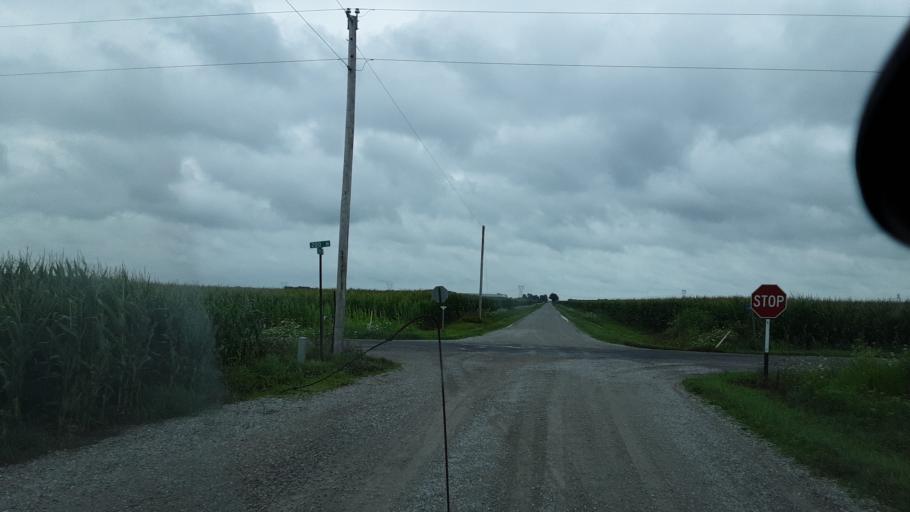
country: US
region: Indiana
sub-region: Wells County
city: Bluffton
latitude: 40.7722
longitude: -85.0713
